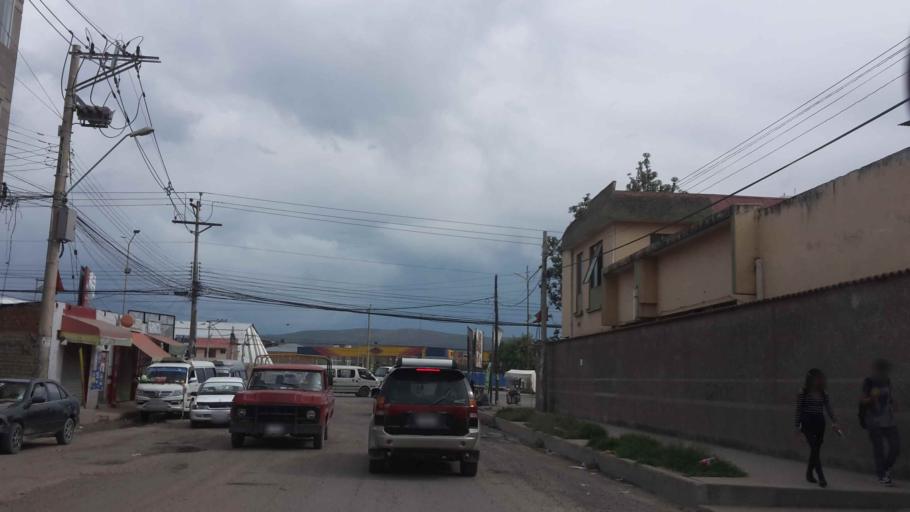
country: BO
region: Cochabamba
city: Cochabamba
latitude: -17.3905
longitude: -66.2508
